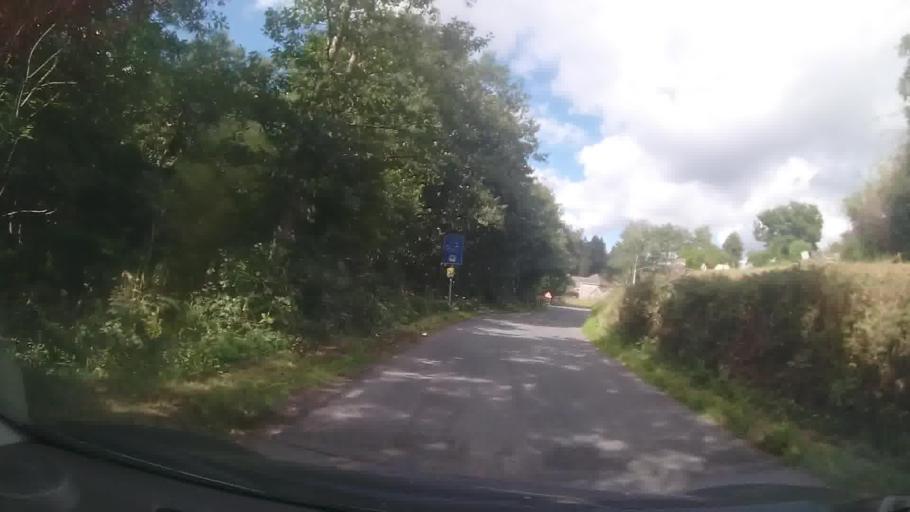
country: GB
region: Wales
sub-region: Merthyr Tydfil County Borough
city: Merthyr Tydfil
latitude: 51.7923
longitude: -3.3641
